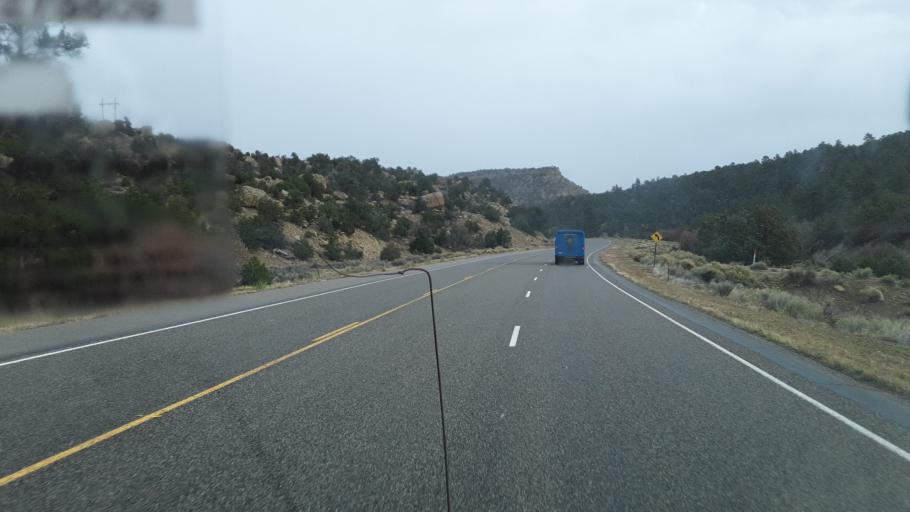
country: US
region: New Mexico
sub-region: Rio Arriba County
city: Tierra Amarilla
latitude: 36.4061
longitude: -106.4909
